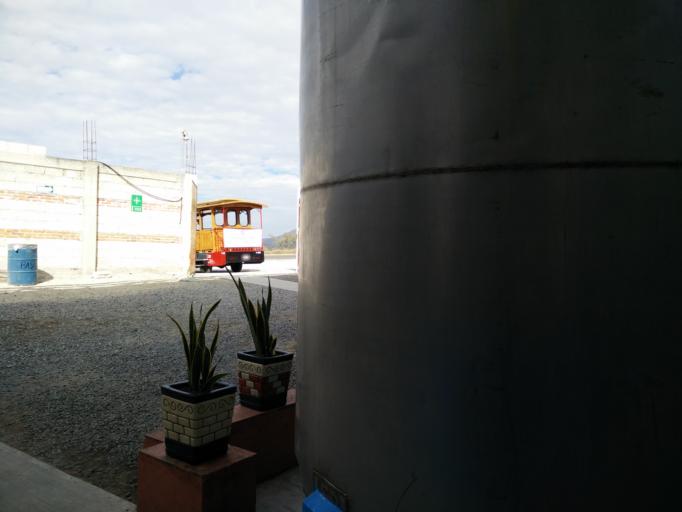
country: MX
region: Queretaro
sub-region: Tequisquiapan
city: Tequisquiapan
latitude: 20.5353
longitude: -99.8787
